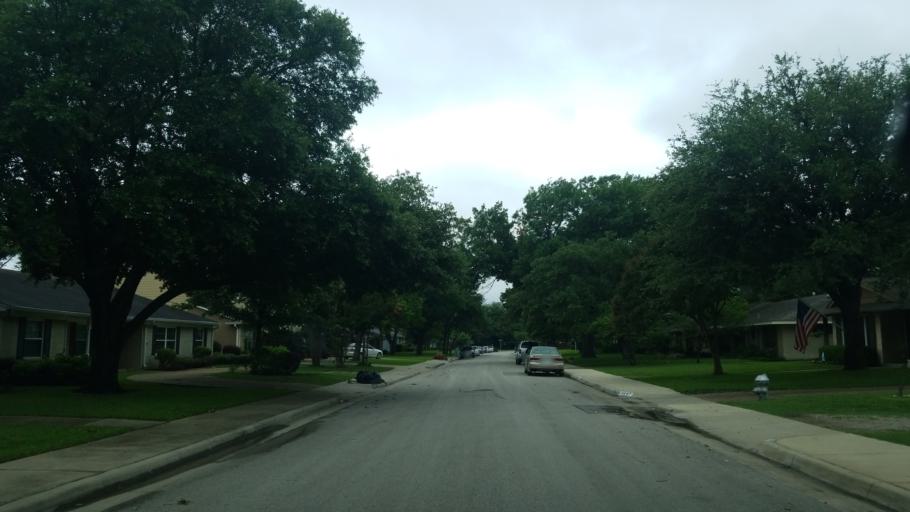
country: US
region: Texas
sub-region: Dallas County
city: Farmers Branch
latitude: 32.8932
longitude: -96.8673
